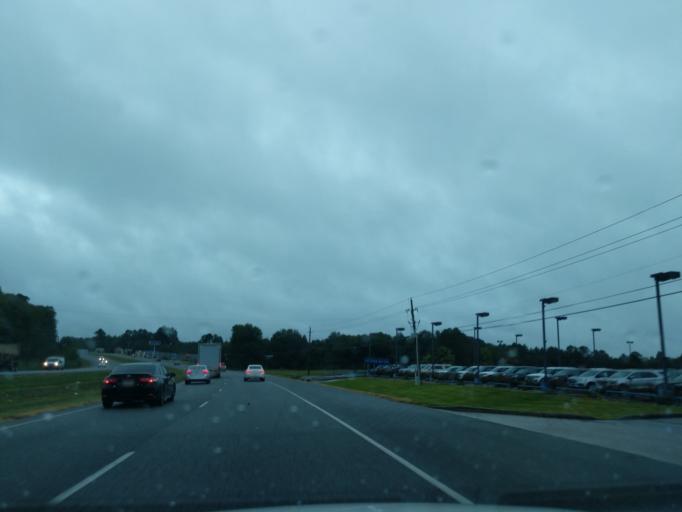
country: US
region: Texas
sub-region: Angelina County
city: Lufkin
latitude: 31.3430
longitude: -94.6913
